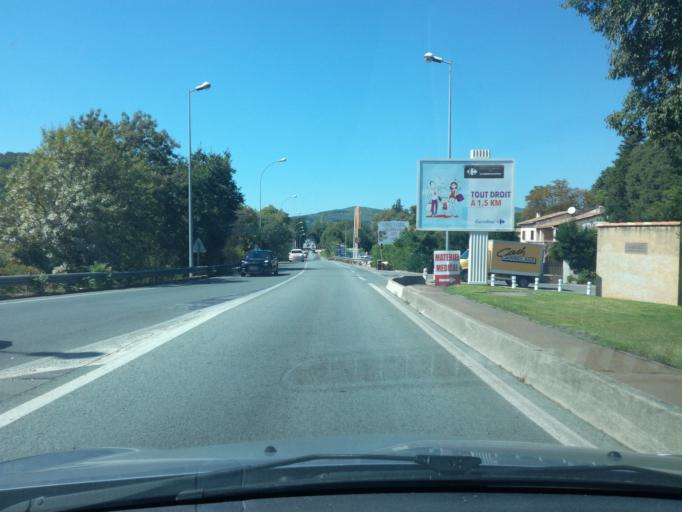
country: FR
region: Provence-Alpes-Cote d'Azur
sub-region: Departement du Var
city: Draguignan
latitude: 43.5202
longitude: 6.4721
